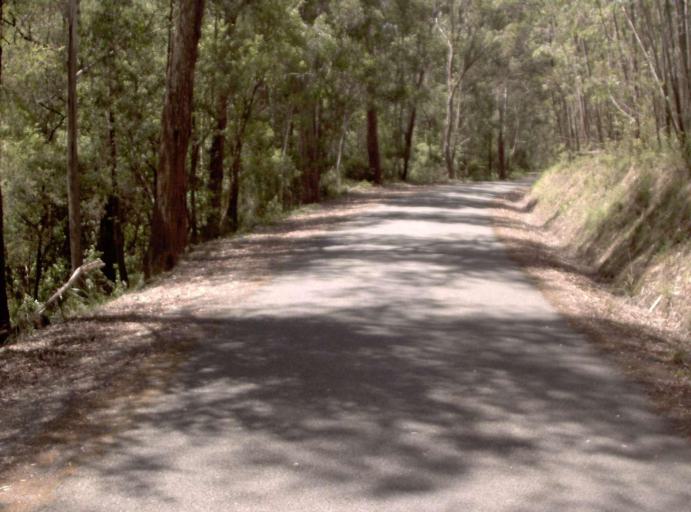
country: AU
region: New South Wales
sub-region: Bombala
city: Bombala
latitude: -37.4367
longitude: 148.9847
